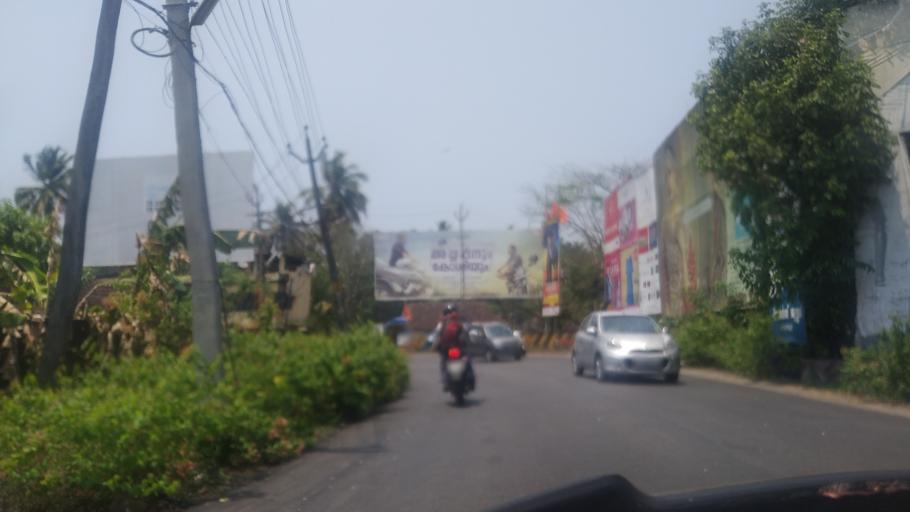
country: IN
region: Kerala
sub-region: Thrissur District
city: Kodungallur
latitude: 10.2481
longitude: 76.1886
